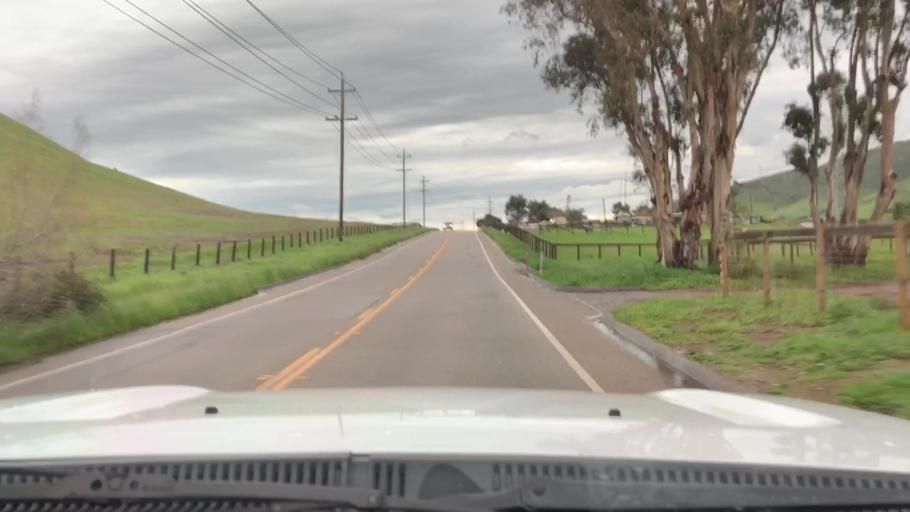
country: US
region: California
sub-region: San Luis Obispo County
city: San Luis Obispo
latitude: 35.2521
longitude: -120.6266
